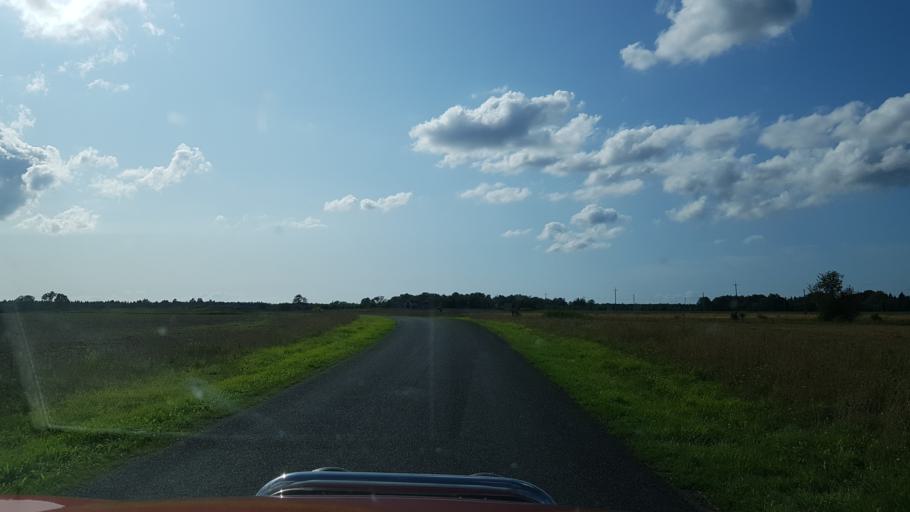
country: EE
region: Harju
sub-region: Paldiski linn
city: Paldiski
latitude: 59.1992
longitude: 23.9535
